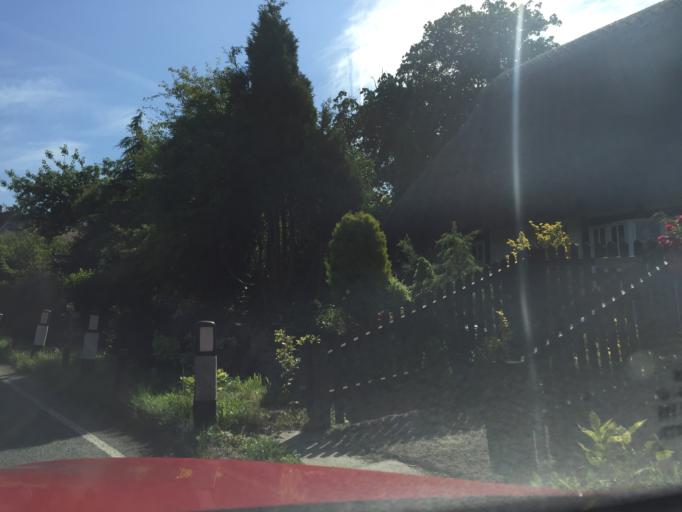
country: GB
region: England
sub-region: Gloucestershire
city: Stonehouse
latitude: 51.8121
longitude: -2.2981
